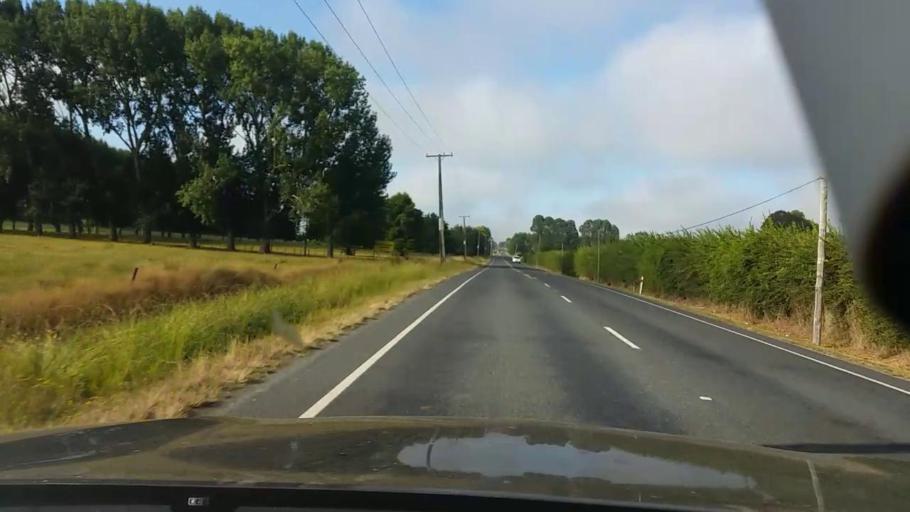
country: NZ
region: Waikato
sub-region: Hamilton City
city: Hamilton
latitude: -37.6014
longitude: 175.3521
